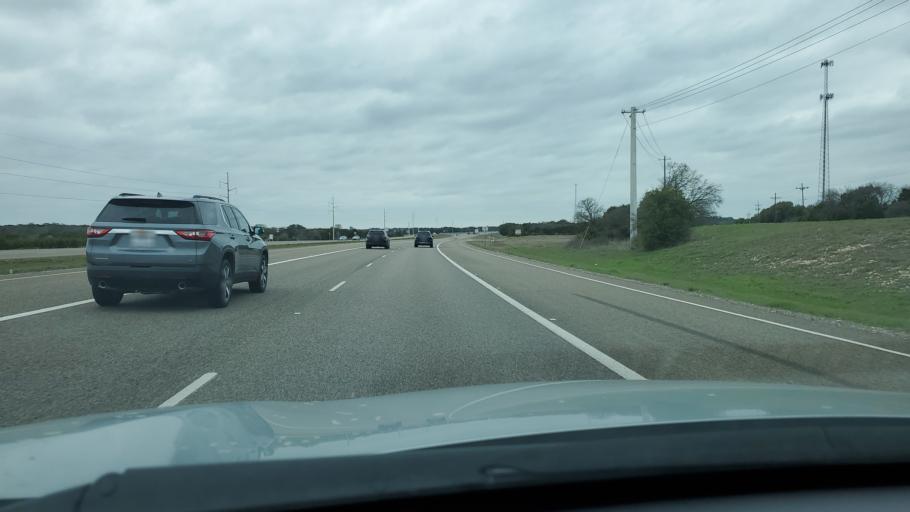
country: US
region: Texas
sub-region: Williamson County
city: Serenada
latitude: 30.7631
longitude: -97.7456
